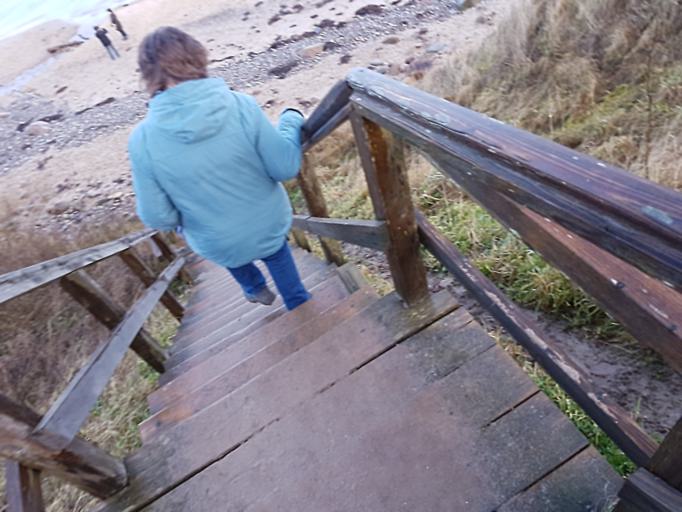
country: DE
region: Schleswig-Holstein
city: Strande
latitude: 54.4771
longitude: 10.1512
